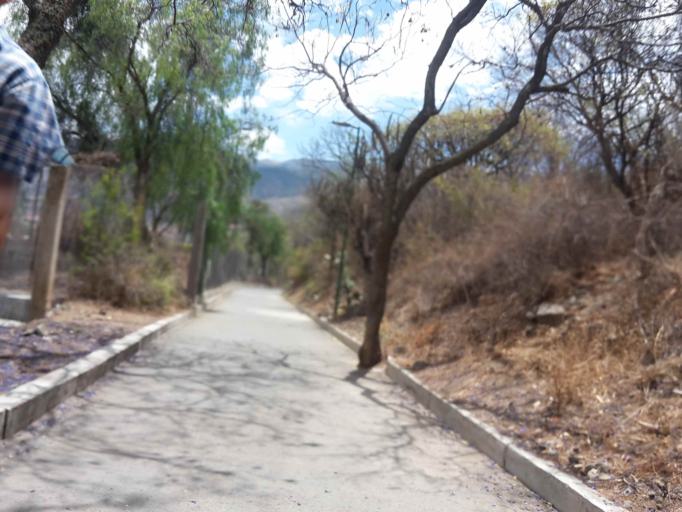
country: BO
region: Cochabamba
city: Cochabamba
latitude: -17.3796
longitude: -66.1387
